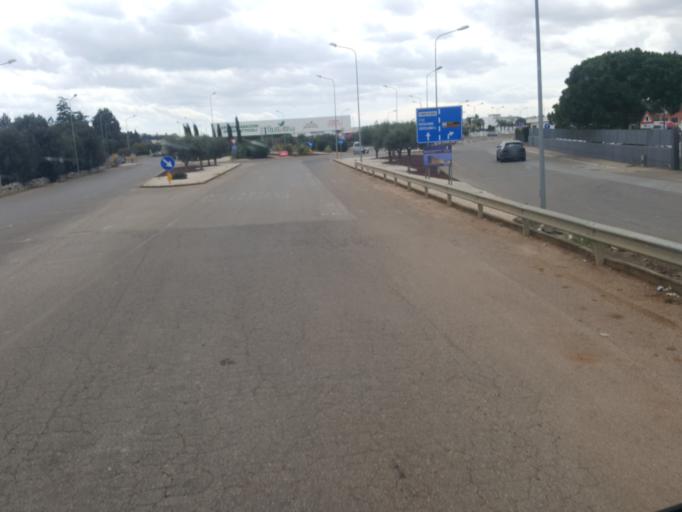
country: IT
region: Apulia
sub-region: Provincia di Bari
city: Conversano
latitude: 40.9812
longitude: 17.1188
